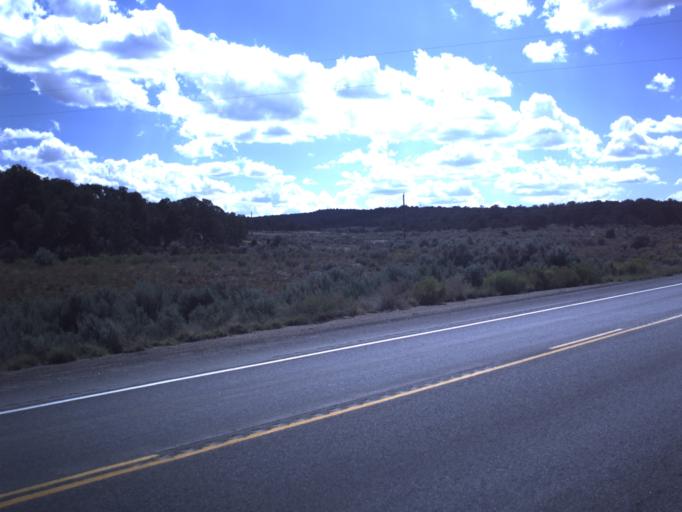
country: US
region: Utah
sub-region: Duchesne County
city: Duchesne
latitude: 40.1806
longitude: -110.6239
